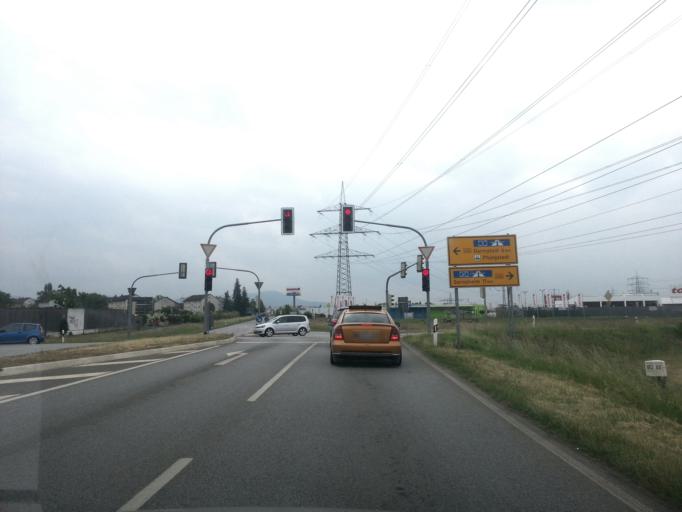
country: DE
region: Hesse
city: Pfungstadt
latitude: 49.8136
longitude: 8.5882
